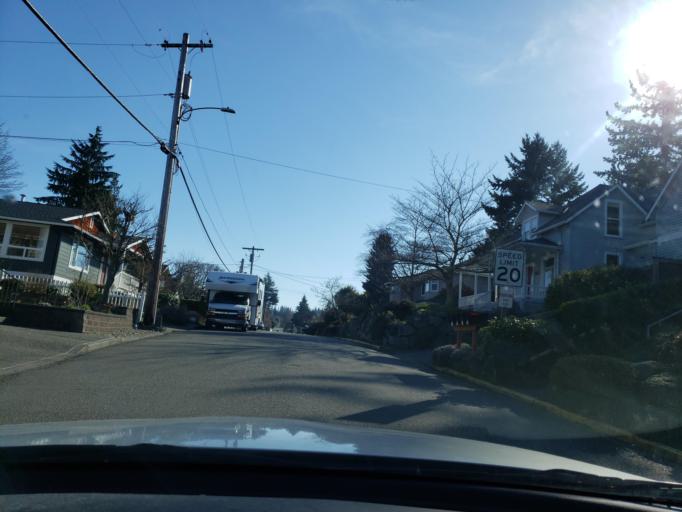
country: US
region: Washington
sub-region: Snohomish County
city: Edmonds
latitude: 47.8070
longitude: -122.3742
